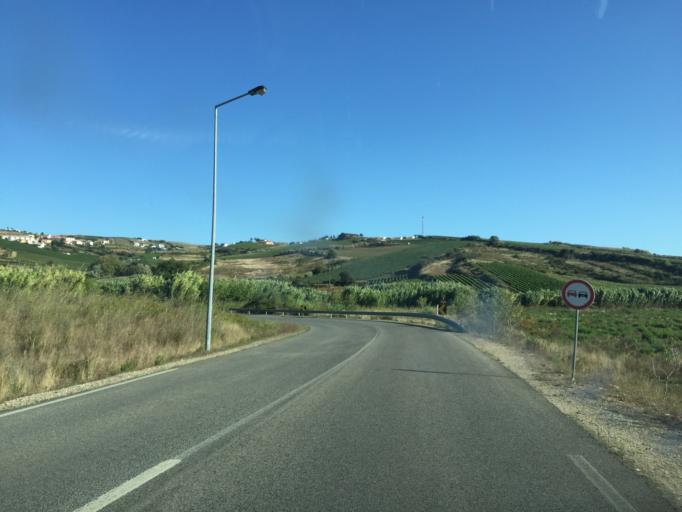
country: PT
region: Lisbon
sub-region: Torres Vedras
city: Torres Vedras
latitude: 39.0959
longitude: -9.2898
